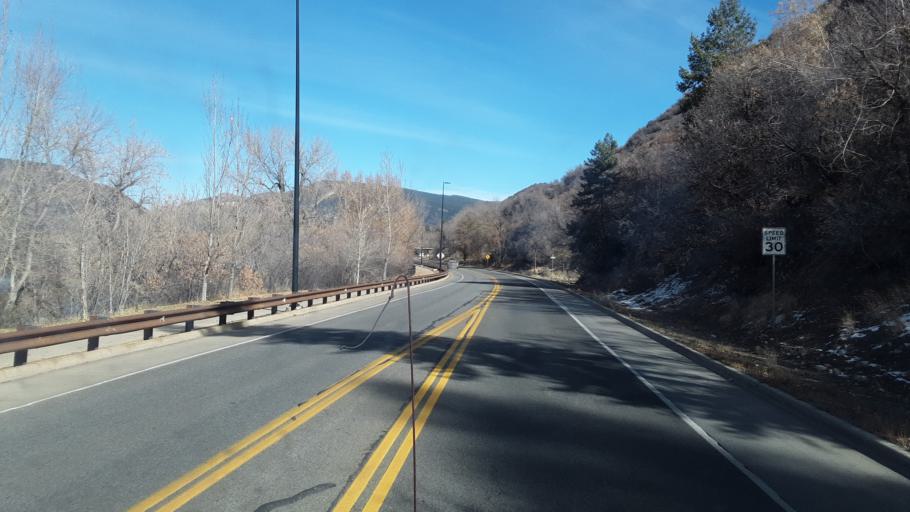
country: US
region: Colorado
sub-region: La Plata County
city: Durango
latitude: 37.2801
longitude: -107.8735
